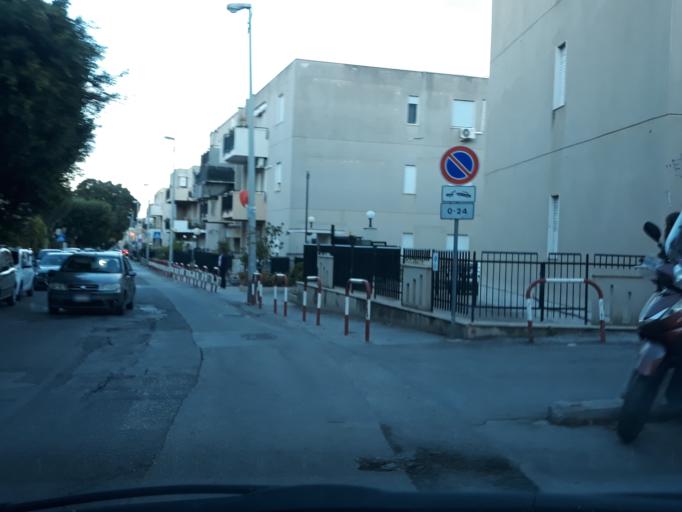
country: IT
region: Sicily
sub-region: Palermo
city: Villa Ciambra
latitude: 38.0913
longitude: 13.3327
